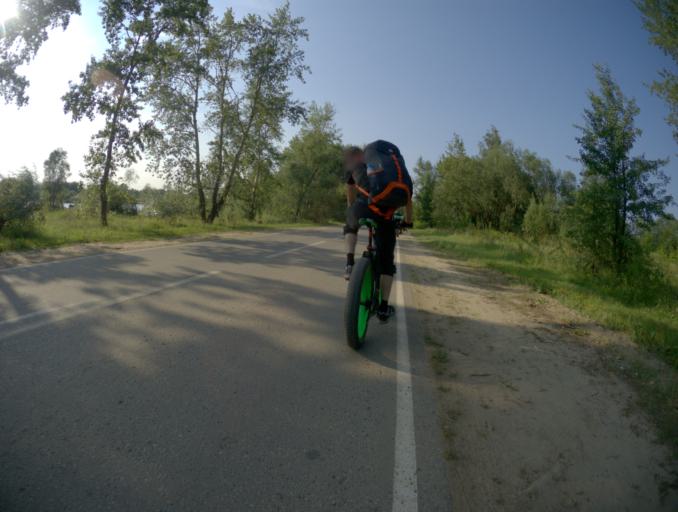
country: RU
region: Nizjnij Novgorod
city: Bor
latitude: 56.3512
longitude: 44.0525
